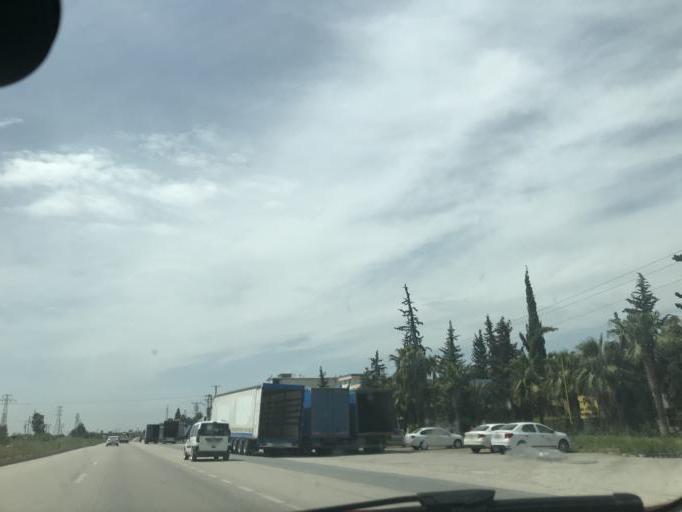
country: TR
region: Adana
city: Yuregir
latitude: 36.9805
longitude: 35.4481
